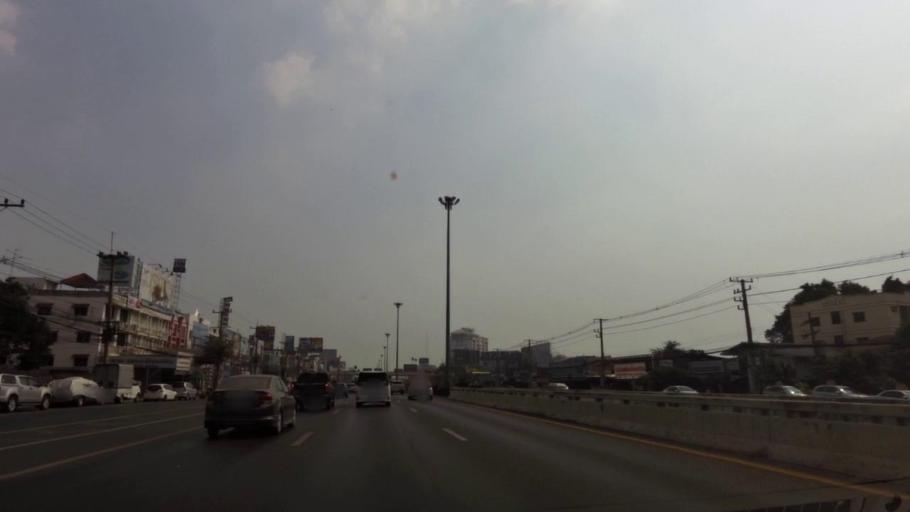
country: TH
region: Phra Nakhon Si Ayutthaya
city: Phra Nakhon Si Ayutthaya
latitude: 14.3497
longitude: 100.6037
